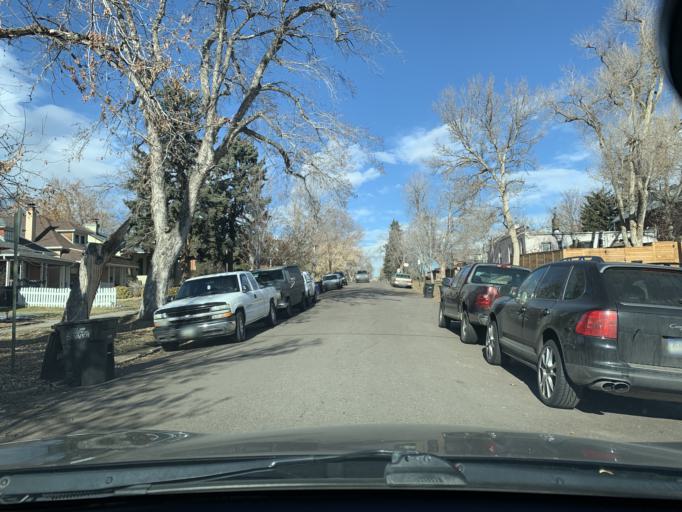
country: US
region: Colorado
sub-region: Jefferson County
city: Edgewater
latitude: 39.7517
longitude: -105.0268
